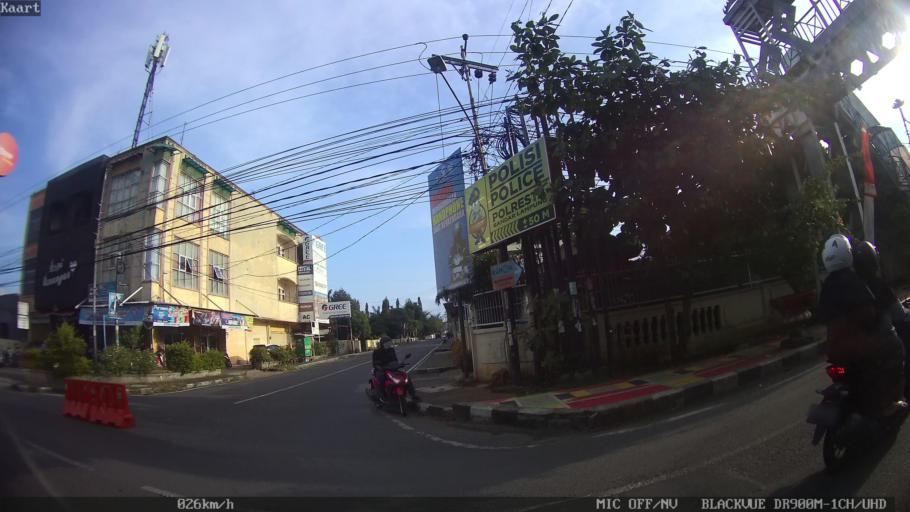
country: ID
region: Lampung
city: Bandarlampung
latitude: -5.4218
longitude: 105.2547
